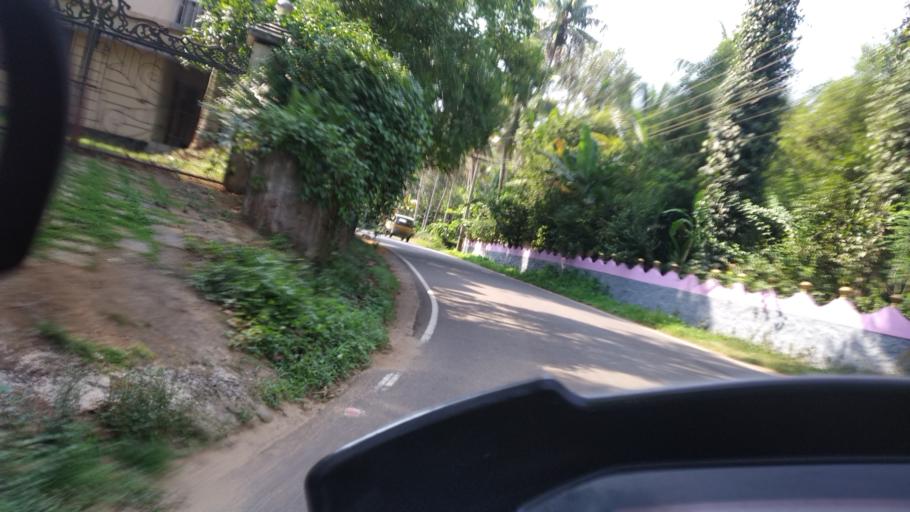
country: IN
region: Kerala
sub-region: Ernakulam
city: Piravam
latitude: 9.8277
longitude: 76.5462
